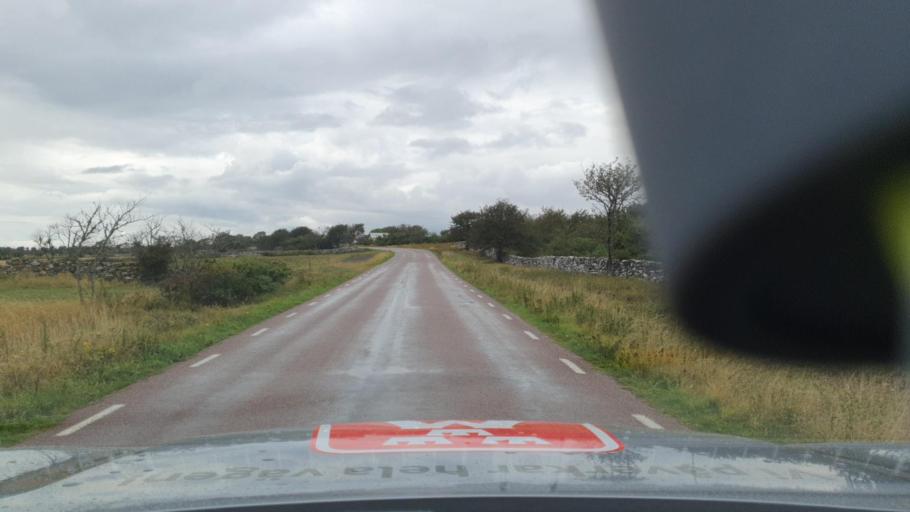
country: SE
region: Gotland
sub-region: Gotland
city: Hemse
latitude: 56.9180
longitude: 18.1464
